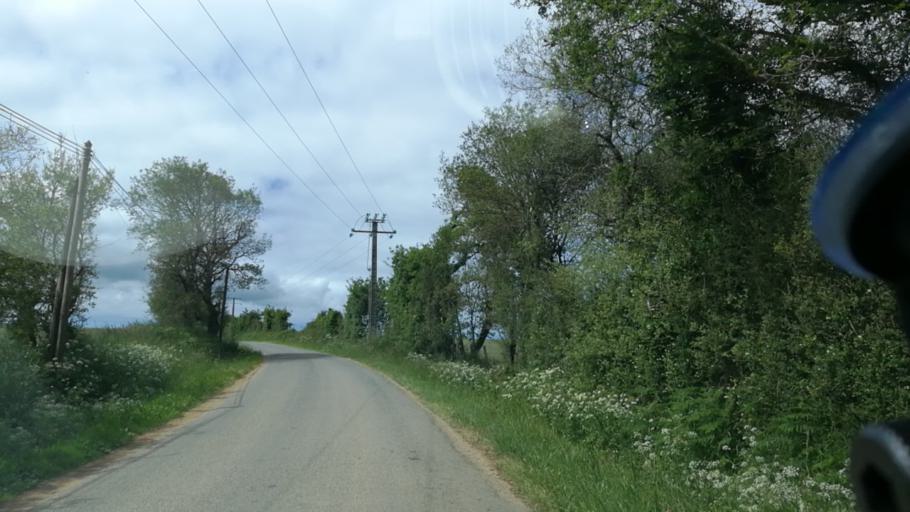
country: FR
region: Pays de la Loire
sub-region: Departement de la Loire-Atlantique
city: Asserac
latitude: 47.4438
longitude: -2.4224
